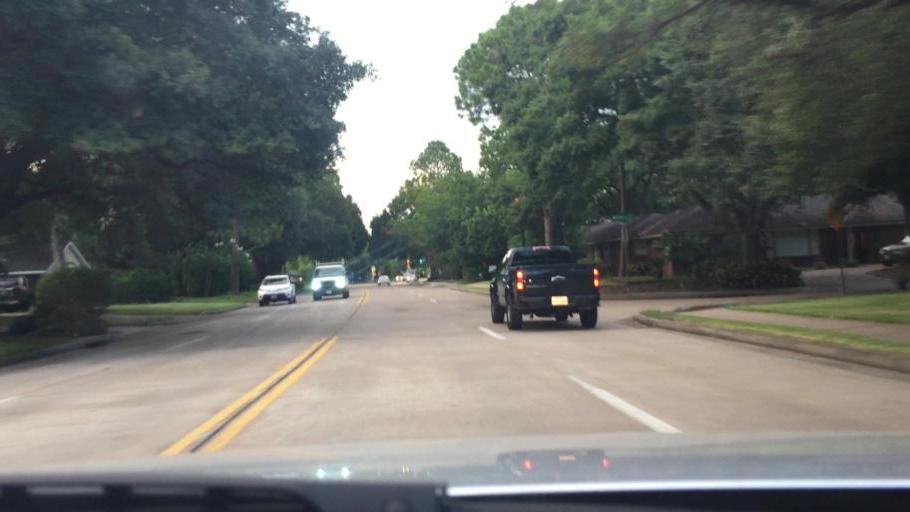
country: US
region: Texas
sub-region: Harris County
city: Hunters Creek Village
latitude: 29.7477
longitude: -95.4772
